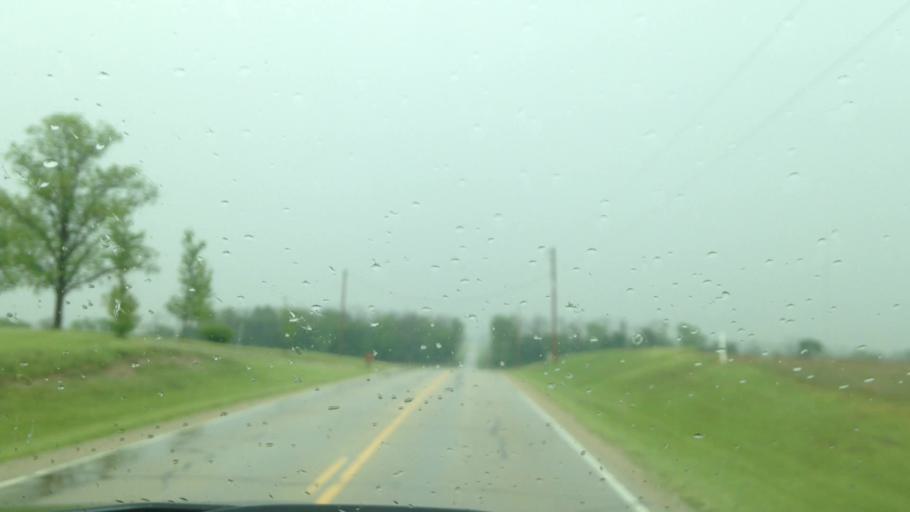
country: US
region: Ohio
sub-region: Darke County
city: Greenville
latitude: 40.1506
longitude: -84.6242
